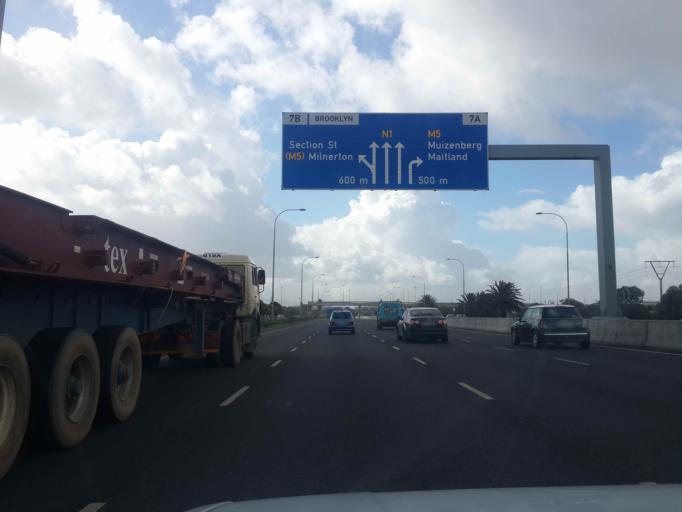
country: ZA
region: Western Cape
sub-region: City of Cape Town
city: Rosebank
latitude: -33.9190
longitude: 18.4731
